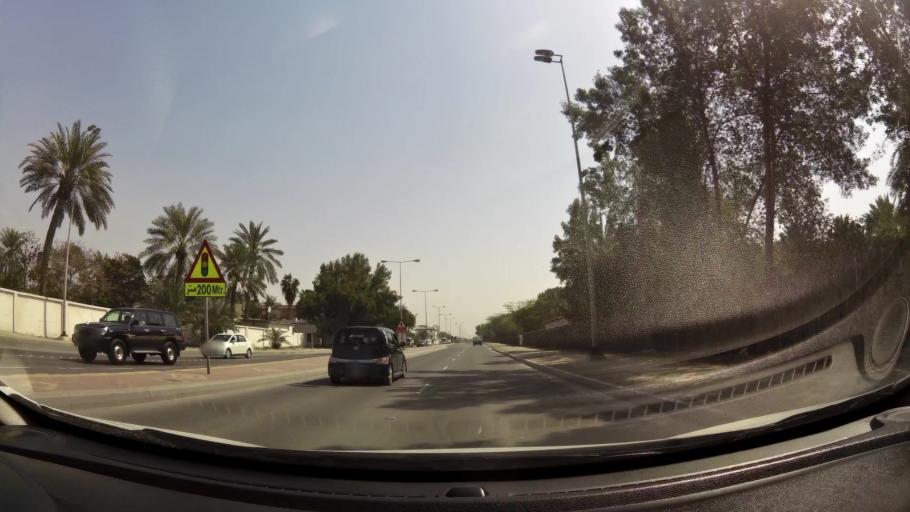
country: BH
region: Manama
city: Jidd Hafs
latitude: 26.2028
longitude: 50.4591
